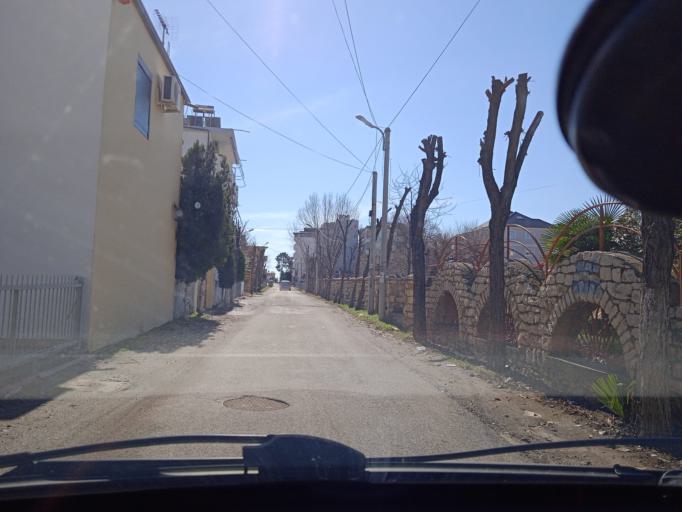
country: AL
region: Shkoder
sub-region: Rrethi i Shkodres
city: Velipoje
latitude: 41.8660
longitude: 19.4227
